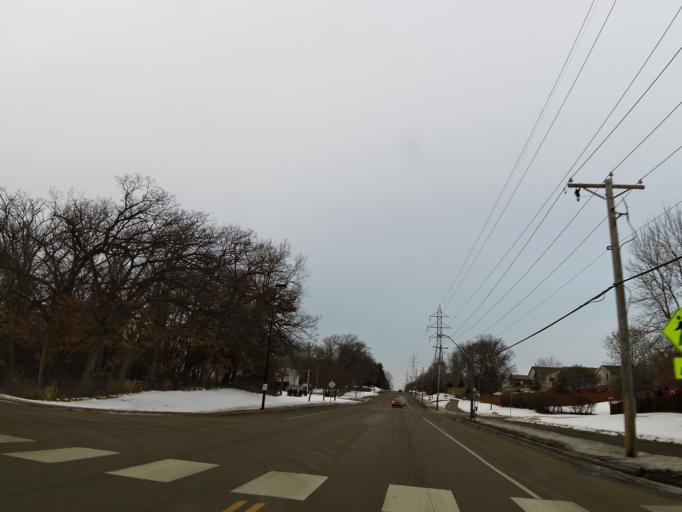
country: US
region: Minnesota
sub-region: Washington County
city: Oakdale
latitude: 44.9786
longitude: -92.9646
